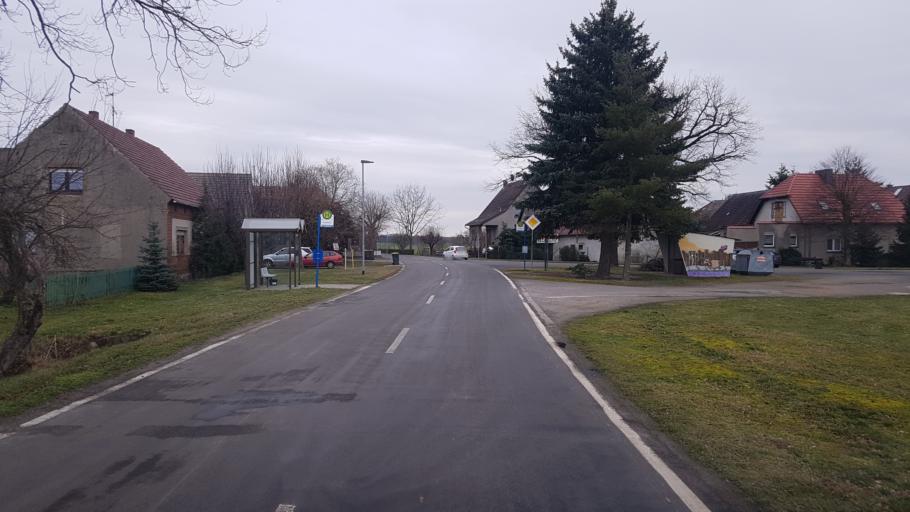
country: DE
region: Brandenburg
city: Sonnewalde
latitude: 51.7077
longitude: 13.6958
